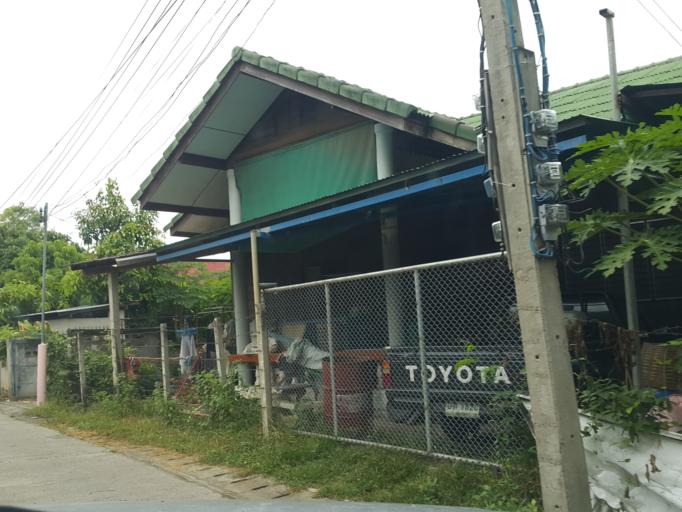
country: TH
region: Chiang Mai
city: San Sai
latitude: 18.8205
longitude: 99.1142
